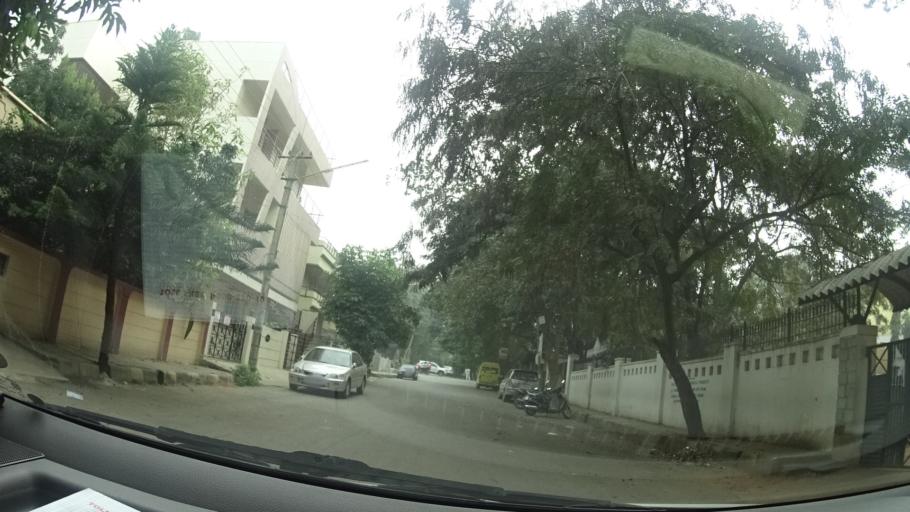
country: IN
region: Karnataka
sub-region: Bangalore Urban
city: Bangalore
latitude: 13.0287
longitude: 77.6278
